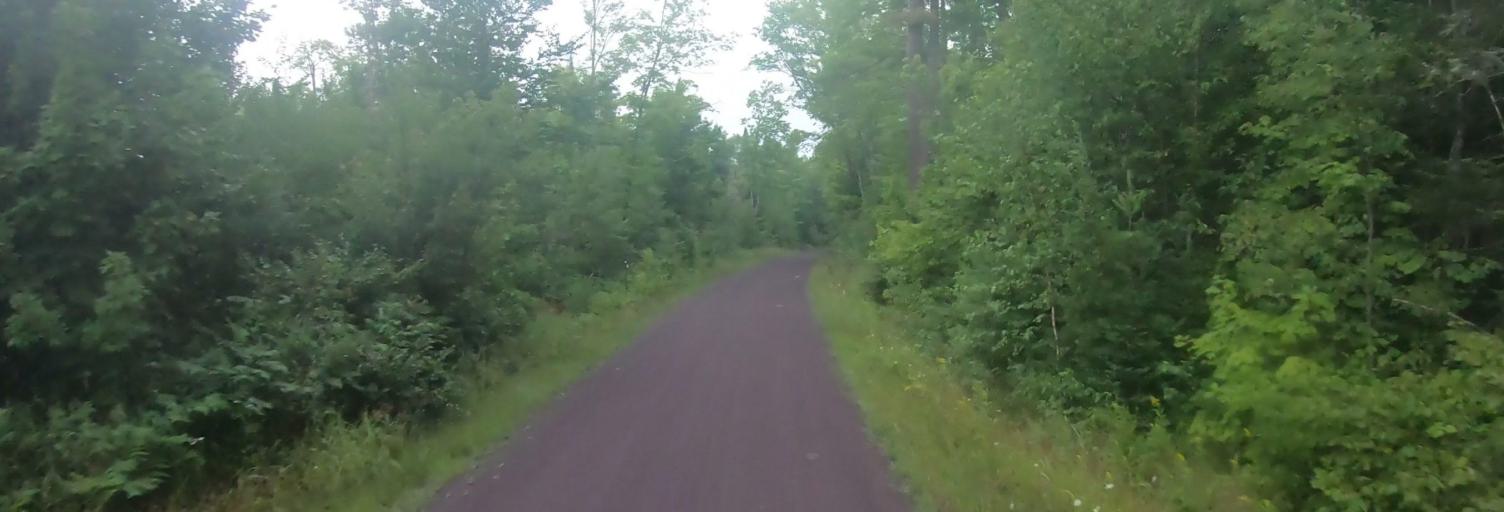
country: US
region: Michigan
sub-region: Keweenaw County
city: Eagle River
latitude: 47.2854
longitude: -88.2557
